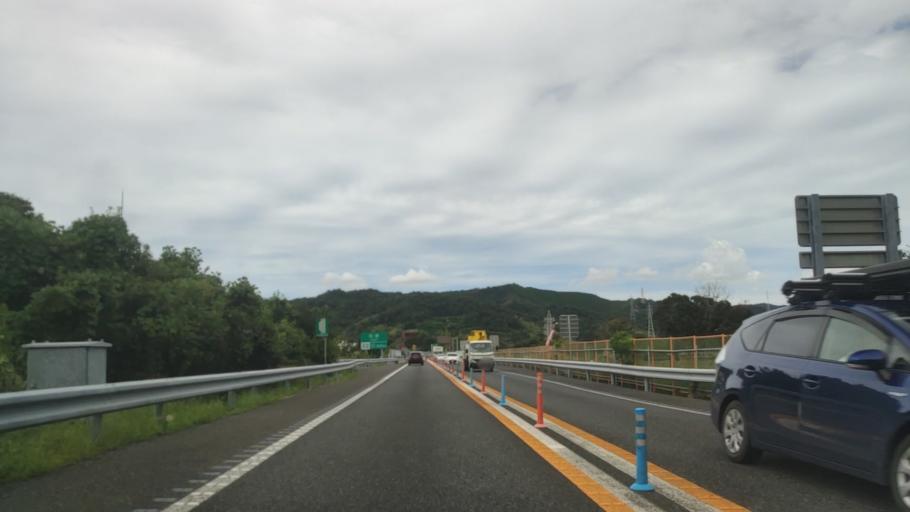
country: JP
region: Wakayama
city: Gobo
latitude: 33.8202
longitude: 135.2241
